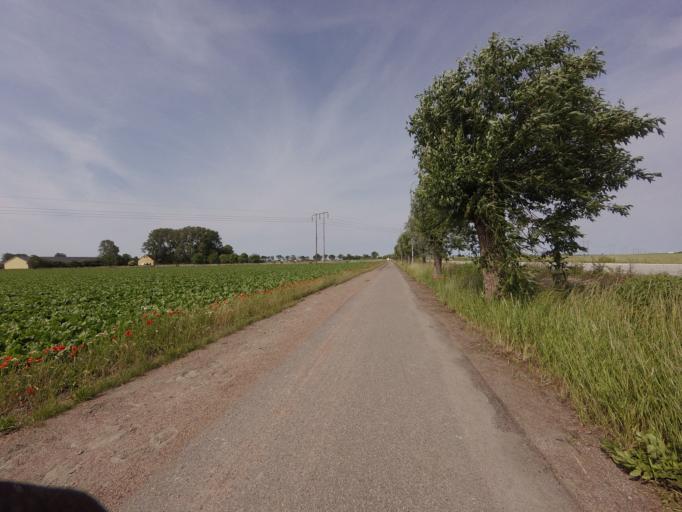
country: SE
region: Skane
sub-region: Malmo
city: Bunkeflostrand
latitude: 55.5283
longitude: 12.9660
